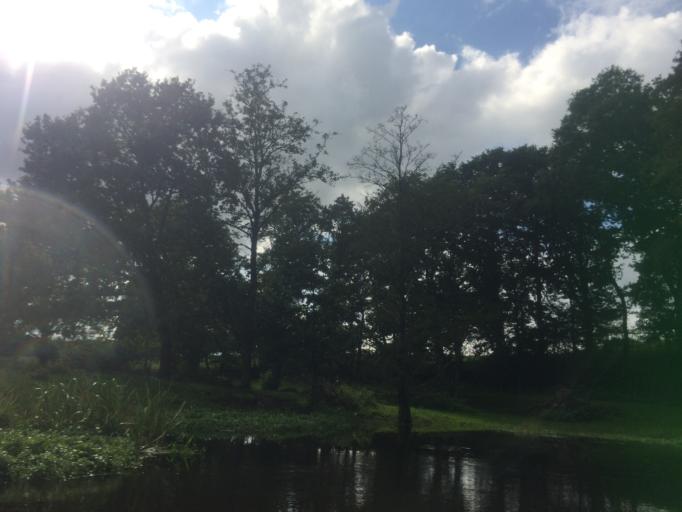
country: DK
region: South Denmark
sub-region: Vejle Kommune
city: Egtved
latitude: 55.6524
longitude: 9.3098
